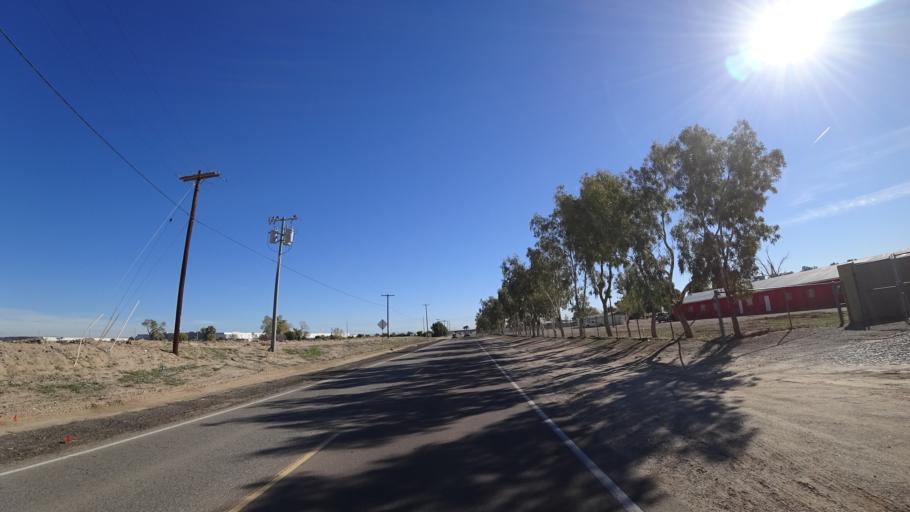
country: US
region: Arizona
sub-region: Maricopa County
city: Citrus Park
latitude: 33.4937
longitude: -112.4304
